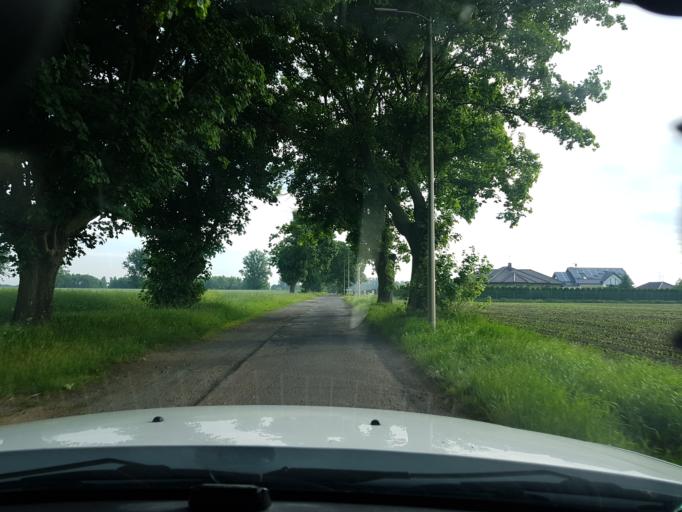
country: PL
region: West Pomeranian Voivodeship
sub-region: Powiat stargardzki
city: Stargard Szczecinski
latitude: 53.3128
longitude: 15.1241
